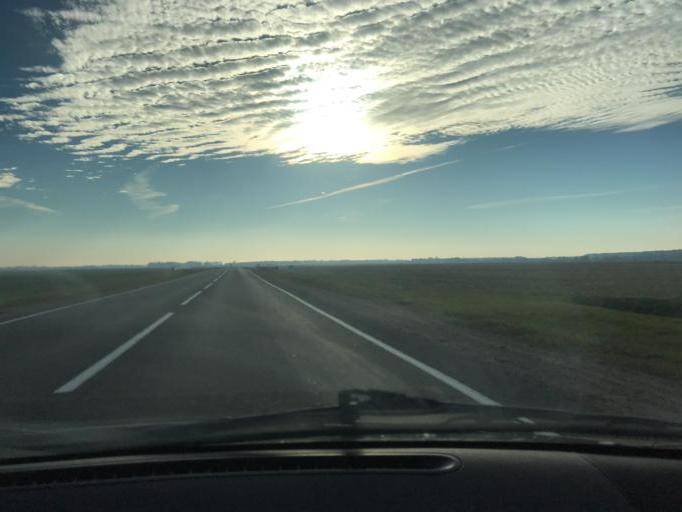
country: BY
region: Brest
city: Drahichyn
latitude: 52.2168
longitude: 25.1792
